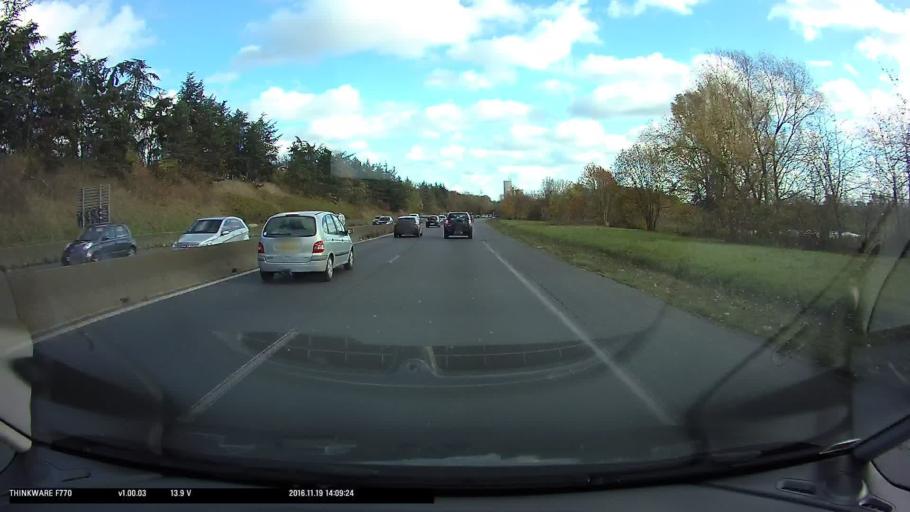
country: FR
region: Ile-de-France
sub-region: Departement du Val-d'Oise
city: Osny
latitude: 49.0543
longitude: 2.0572
